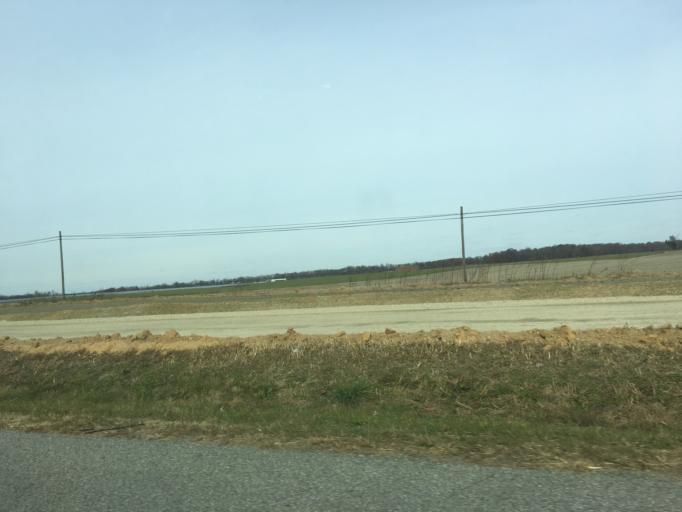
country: US
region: Maryland
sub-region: Queen Anne's County
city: Centreville
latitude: 38.9347
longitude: -76.0370
